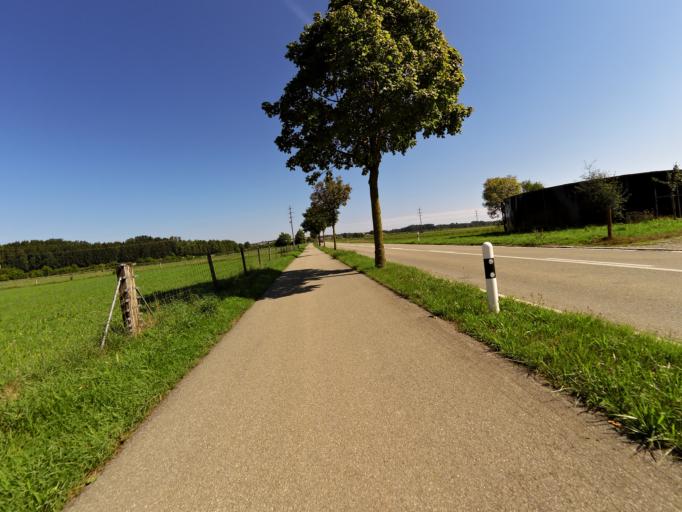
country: CH
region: Thurgau
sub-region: Weinfelden District
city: Maerstetten-Dorf
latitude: 47.6100
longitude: 9.0866
